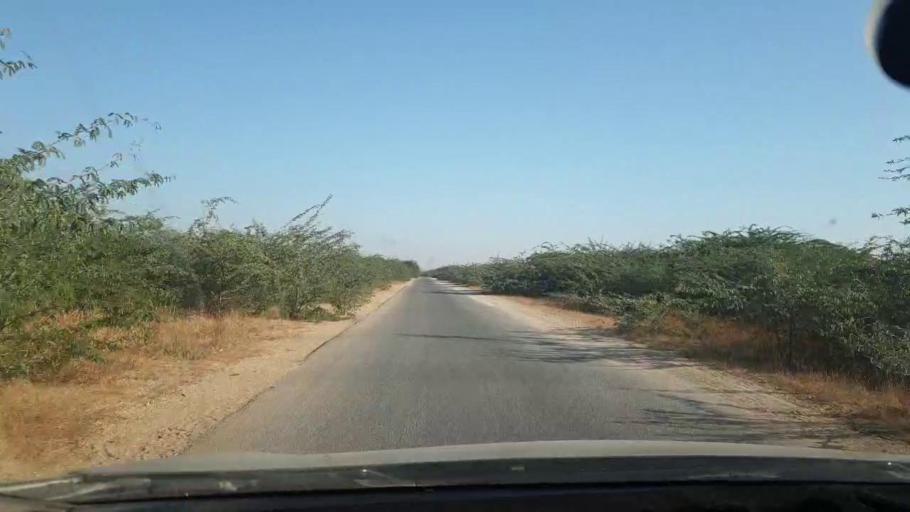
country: PK
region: Sindh
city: Malir Cantonment
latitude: 25.1624
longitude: 67.1950
